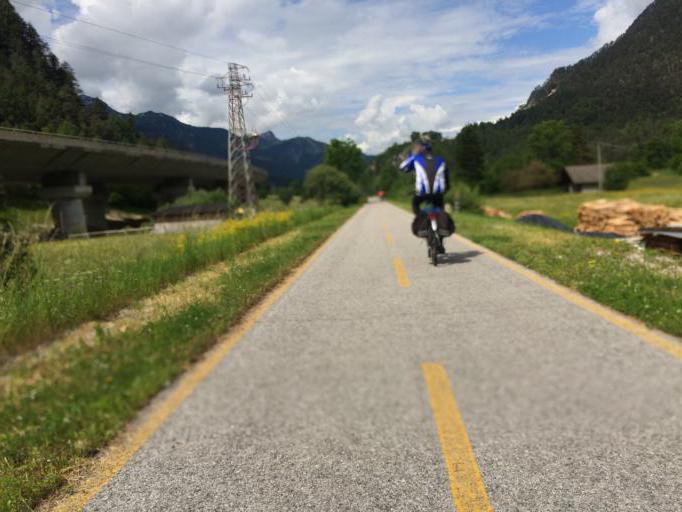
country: IT
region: Friuli Venezia Giulia
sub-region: Provincia di Udine
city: Malborghetto
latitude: 46.5092
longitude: 13.4663
